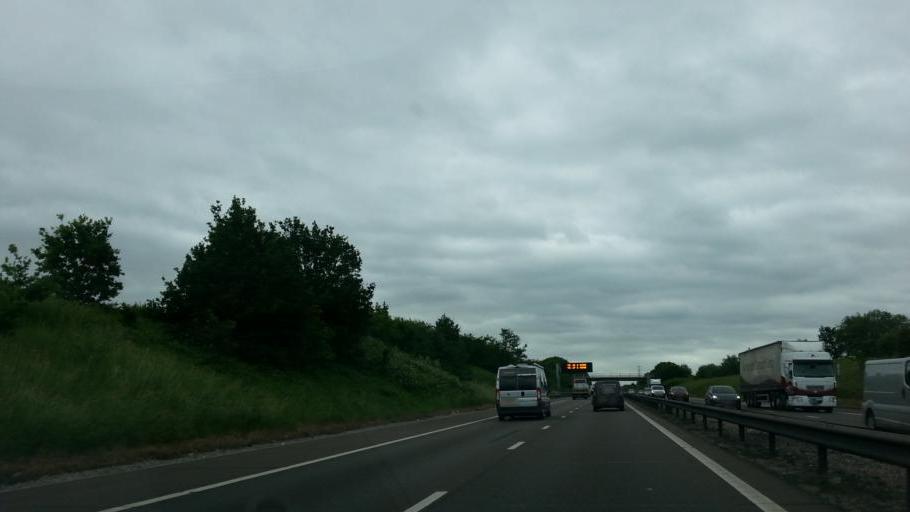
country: GB
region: England
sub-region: Warwickshire
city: Kingsbury
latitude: 52.5566
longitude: -1.7091
